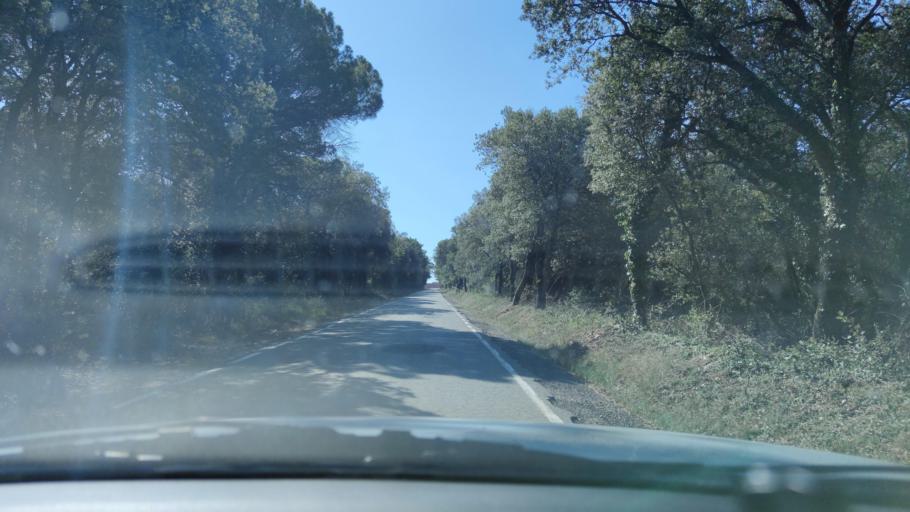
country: ES
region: Catalonia
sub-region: Provincia de Lleida
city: Sant Guim de Freixenet
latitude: 41.6649
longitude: 1.4168
